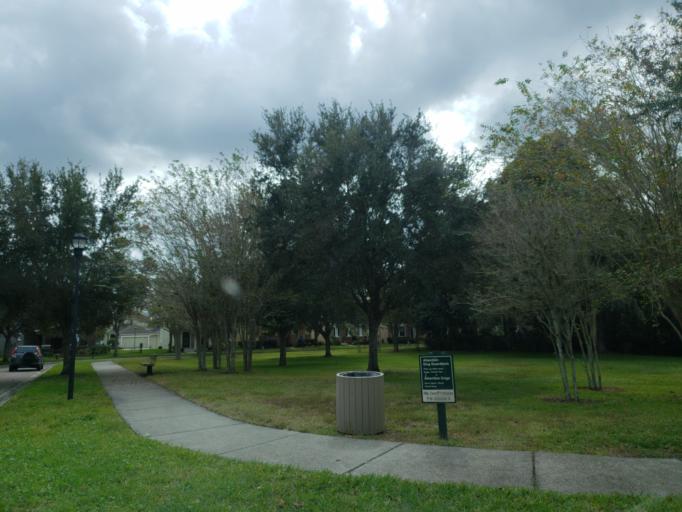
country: US
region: Florida
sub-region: Hillsborough County
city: Fish Hawk
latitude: 27.8442
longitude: -82.2162
